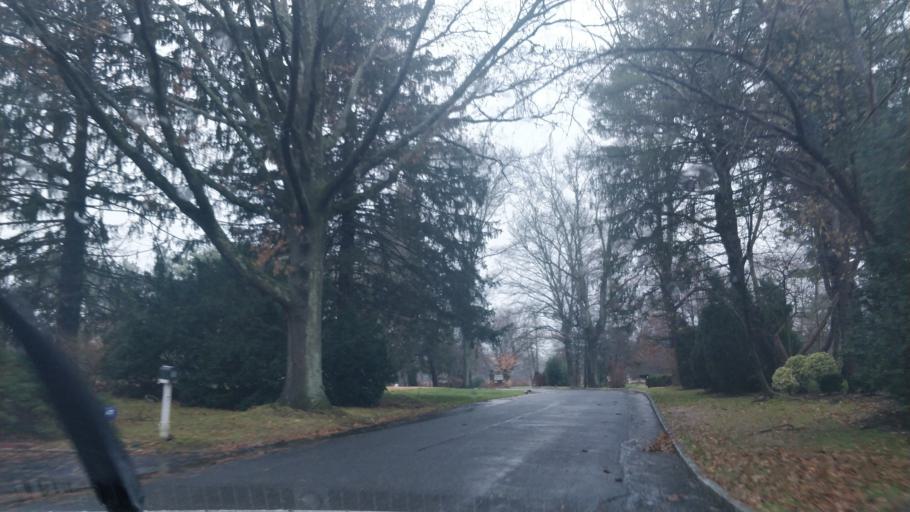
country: US
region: New York
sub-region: Nassau County
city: Old Brookville
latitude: 40.8372
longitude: -73.5999
